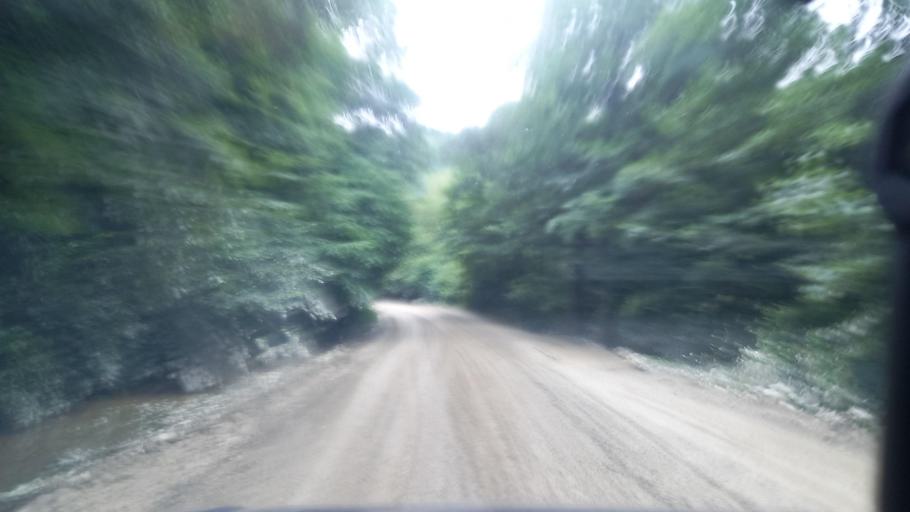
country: RU
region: Karachayevo-Cherkesiya
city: Kurdzhinovo
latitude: 43.9454
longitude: 40.9590
